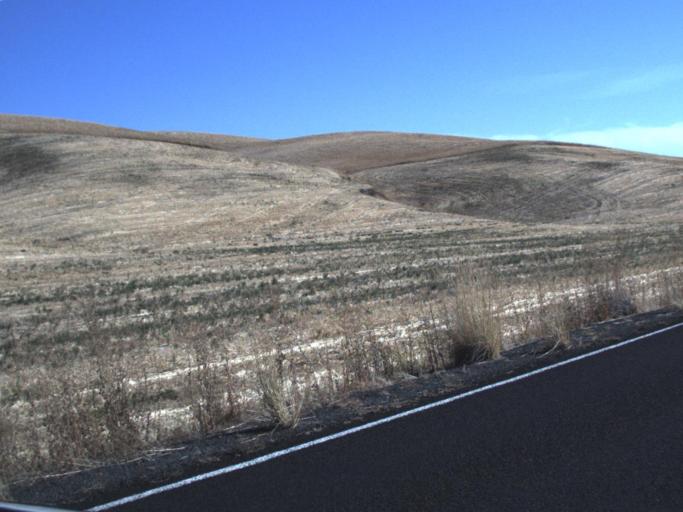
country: US
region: Washington
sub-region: Walla Walla County
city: Walla Walla
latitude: 46.2116
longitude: -118.3908
